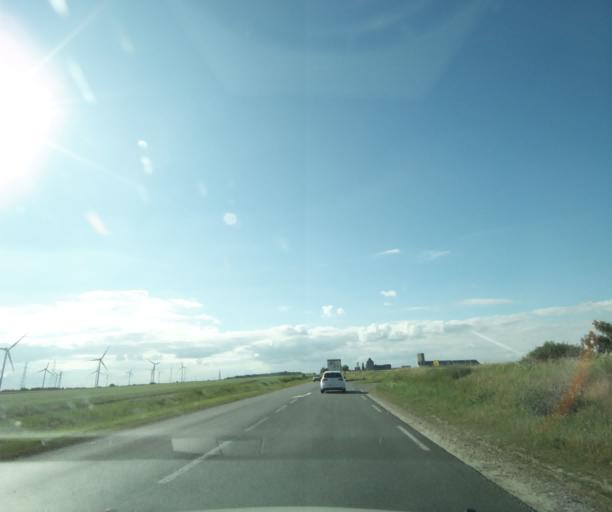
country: FR
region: Centre
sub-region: Departement d'Eure-et-Loir
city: Voves
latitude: 48.3165
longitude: 1.6756
